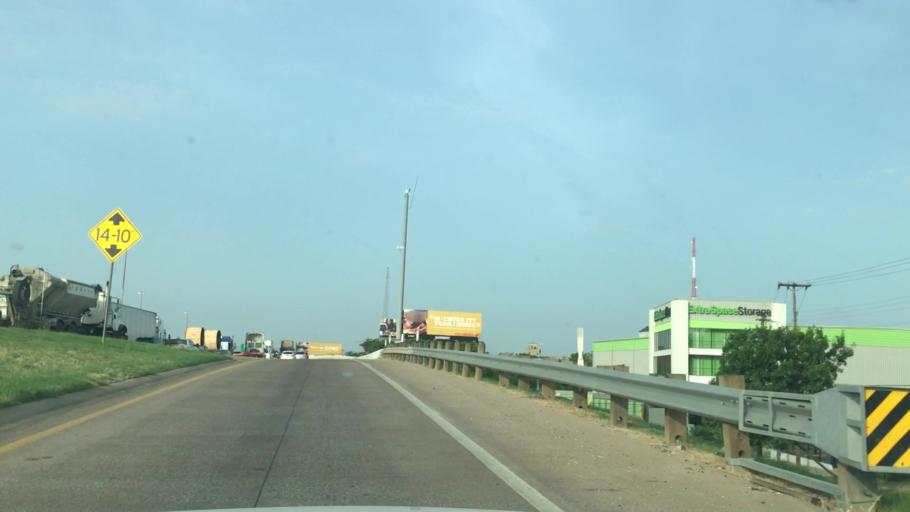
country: US
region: Texas
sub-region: Dallas County
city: Dallas
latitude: 32.7868
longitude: -96.7671
